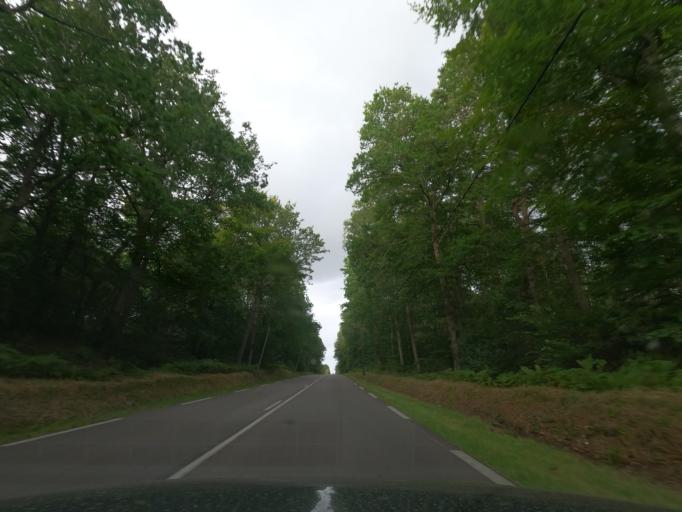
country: FR
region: Haute-Normandie
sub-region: Departement de l'Eure
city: Menneval
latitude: 49.1245
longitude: 0.6335
